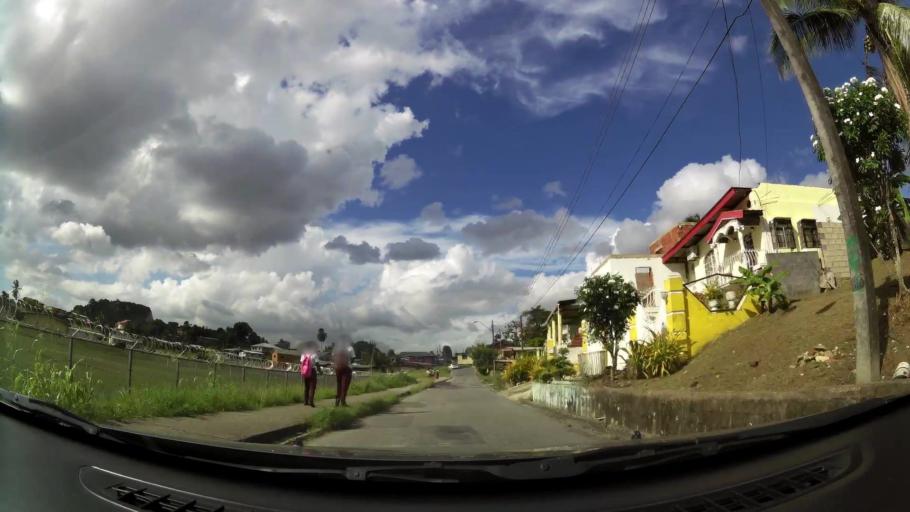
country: TT
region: City of San Fernando
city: Mon Repos
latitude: 10.2723
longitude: -61.4477
